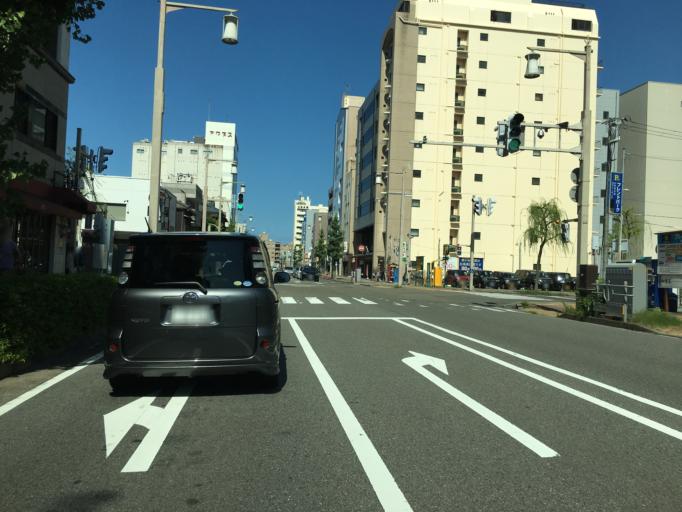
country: JP
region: Niigata
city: Niigata-shi
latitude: 37.9230
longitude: 139.0463
